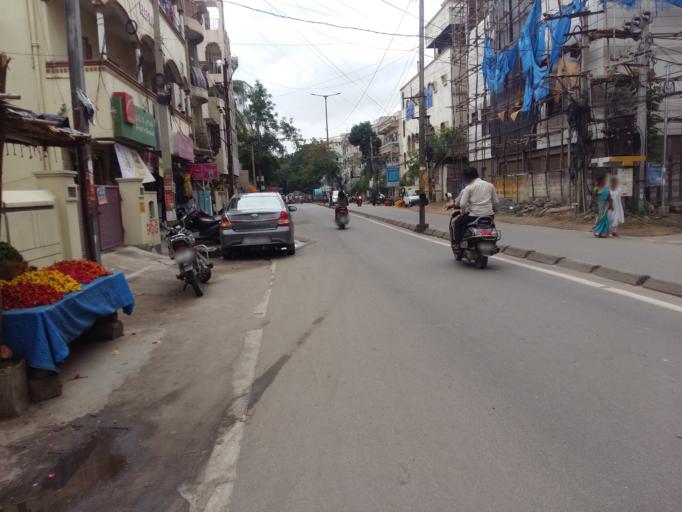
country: IN
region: Telangana
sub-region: Rangareddi
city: Kukatpalli
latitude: 17.4951
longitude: 78.4120
